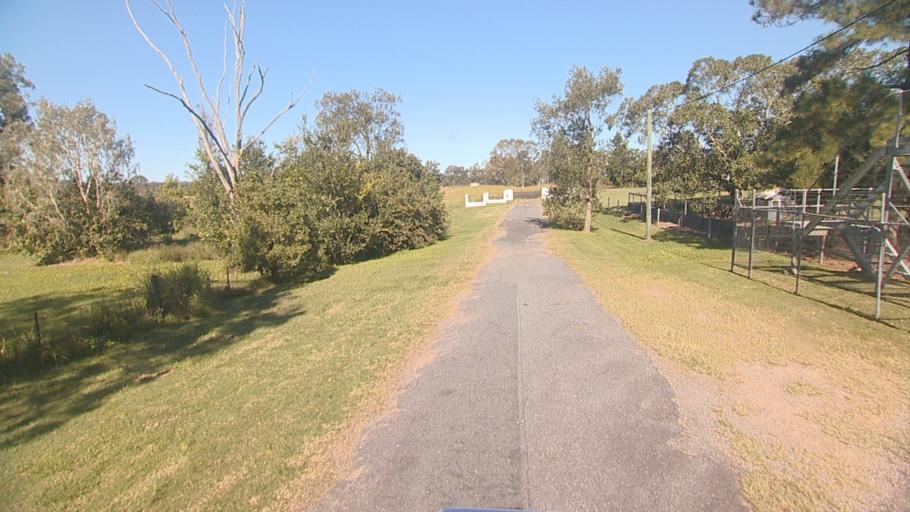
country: AU
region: Queensland
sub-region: Logan
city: Waterford West
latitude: -27.7044
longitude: 153.1409
